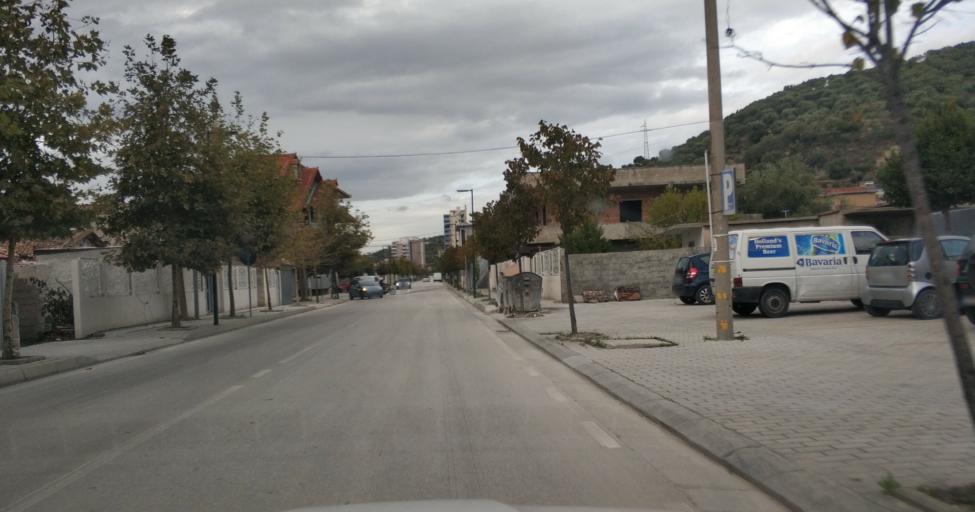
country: AL
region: Vlore
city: Vlore
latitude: 40.4520
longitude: 19.4972
